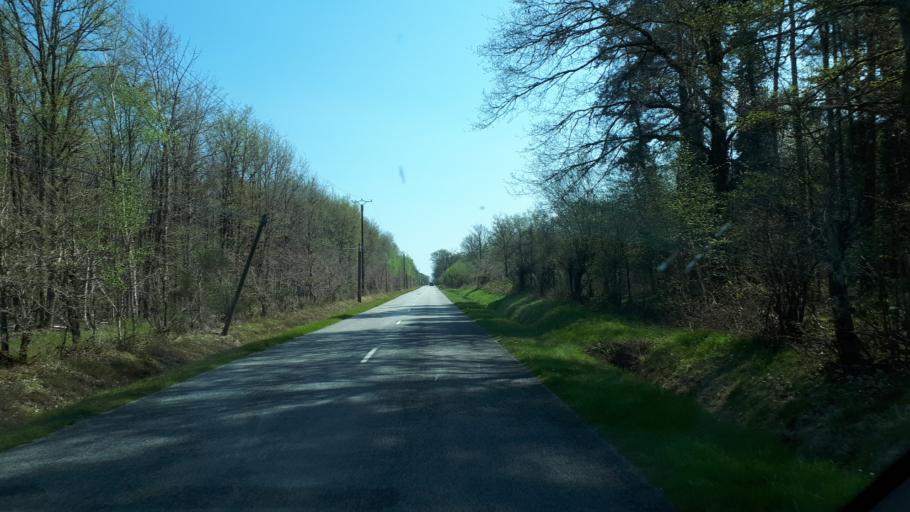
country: FR
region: Centre
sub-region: Departement du Loir-et-Cher
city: Theillay
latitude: 47.3141
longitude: 2.0978
